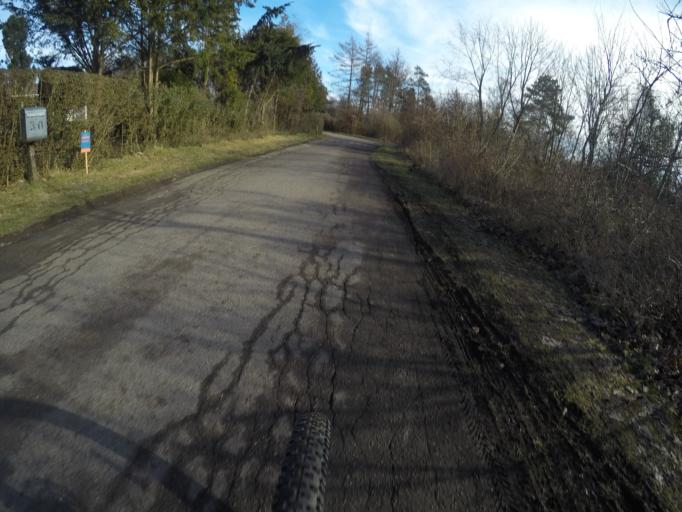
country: DK
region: Capital Region
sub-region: Halsnaes Kommune
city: Liseleje
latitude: 55.9965
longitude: 11.9339
